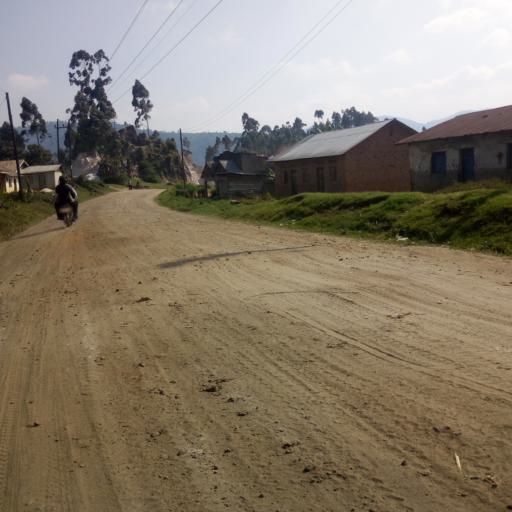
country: UG
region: Western Region
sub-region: Kisoro District
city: Kisoro
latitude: -1.2303
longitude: 29.7109
